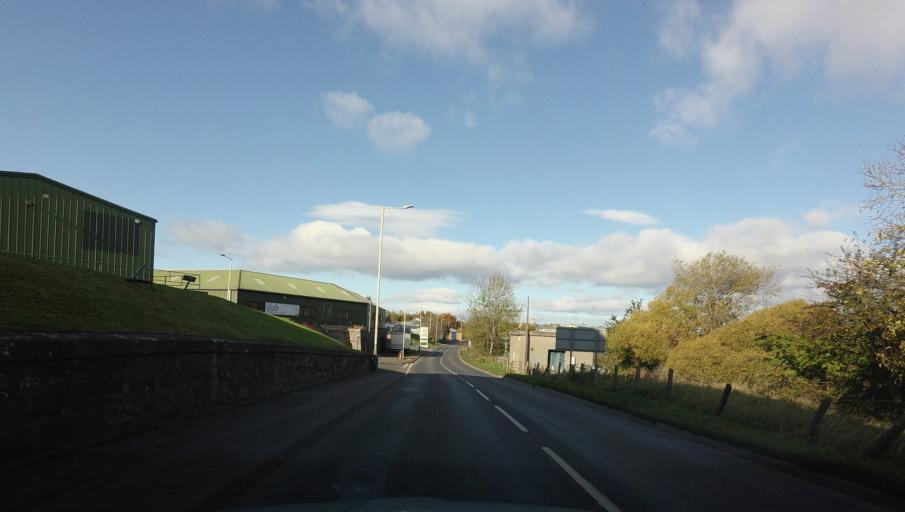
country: GB
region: Scotland
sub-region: Perth and Kinross
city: Perth
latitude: 56.3789
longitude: -3.4282
